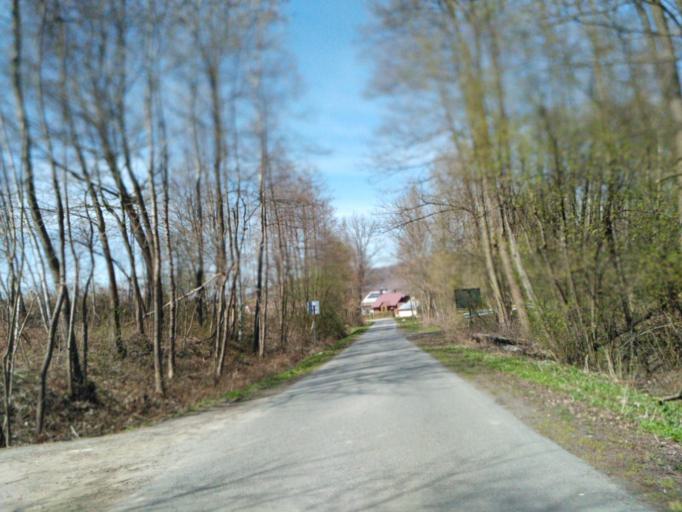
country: PL
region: Subcarpathian Voivodeship
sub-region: Powiat strzyzowski
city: Babica
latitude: 49.9264
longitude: 21.8858
